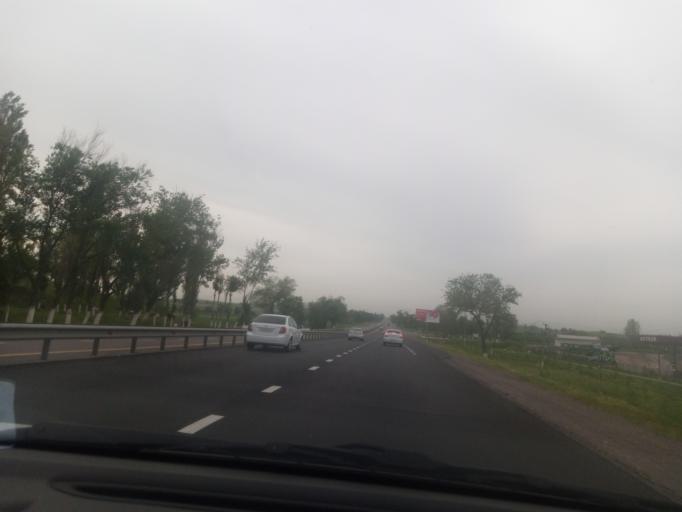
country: UZ
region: Toshkent
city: Tuytepa
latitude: 41.0790
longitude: 69.4711
